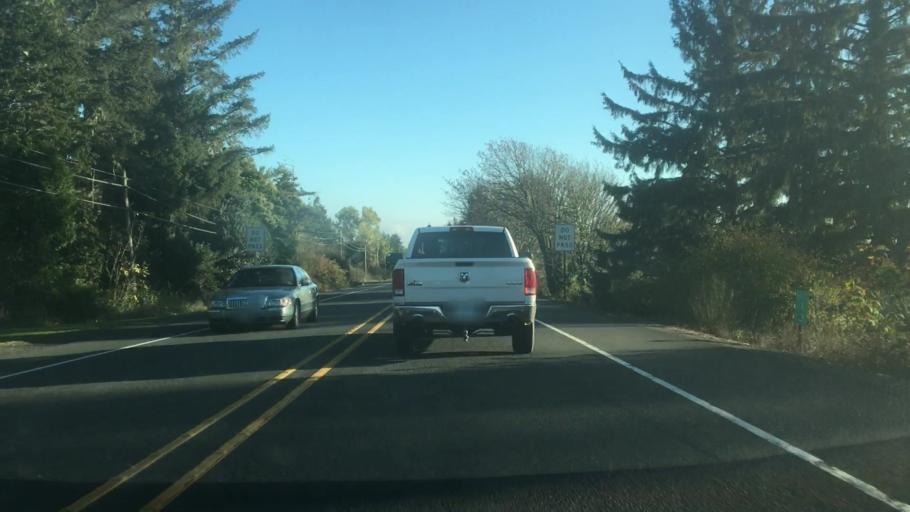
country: US
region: Oregon
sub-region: Clatsop County
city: Warrenton
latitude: 46.1071
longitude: -123.9214
